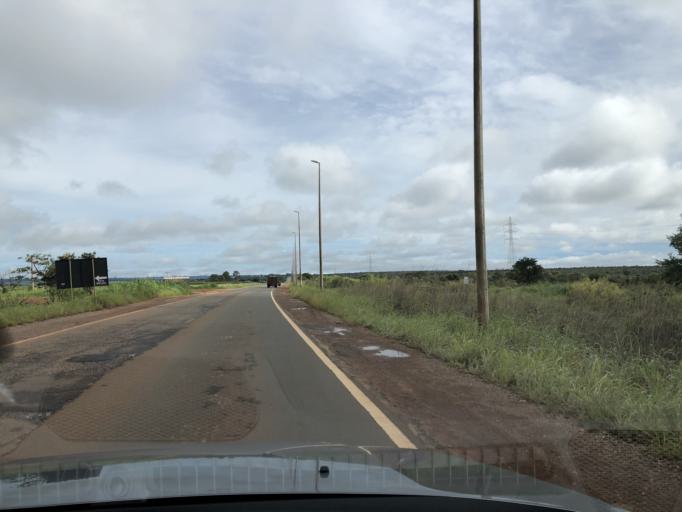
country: BR
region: Federal District
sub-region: Brasilia
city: Brasilia
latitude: -15.7236
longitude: -48.0865
